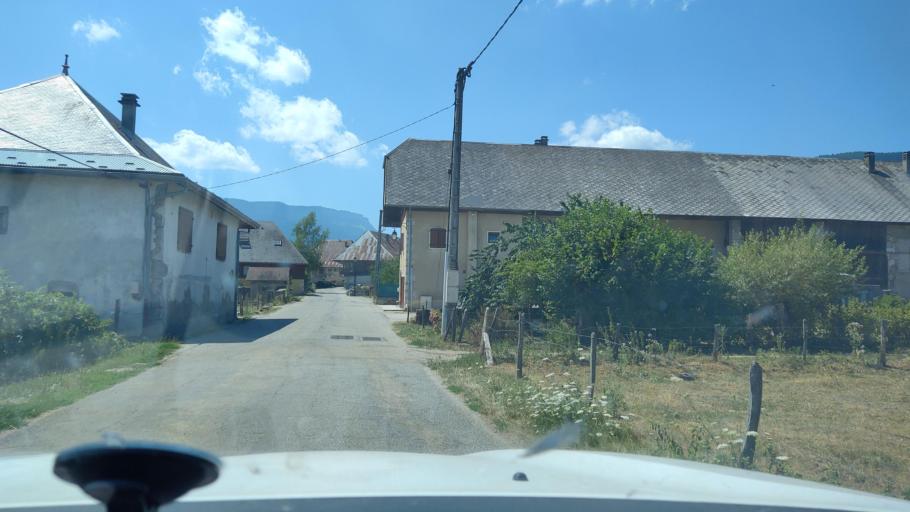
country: FR
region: Rhone-Alpes
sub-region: Departement de la Haute-Savoie
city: Gruffy
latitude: 45.7152
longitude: 6.0877
